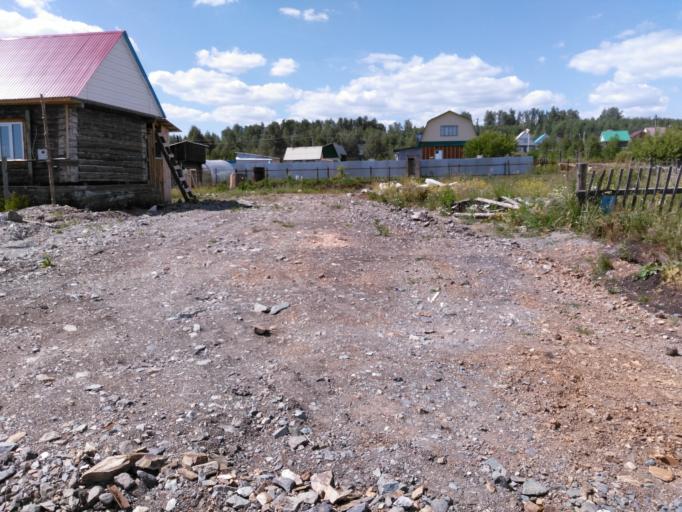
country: RU
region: Bashkortostan
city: Uchaly
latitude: 54.2890
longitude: 59.3578
